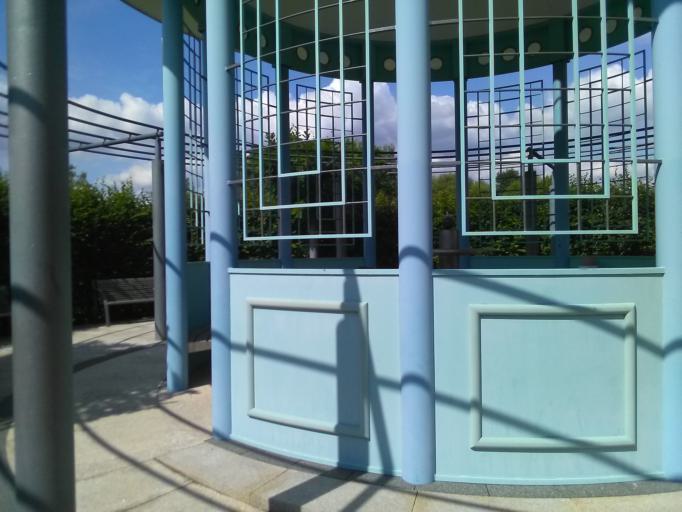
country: DE
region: Bavaria
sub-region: Upper Franconia
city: Bad Staffelstein
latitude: 50.1112
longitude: 10.9862
